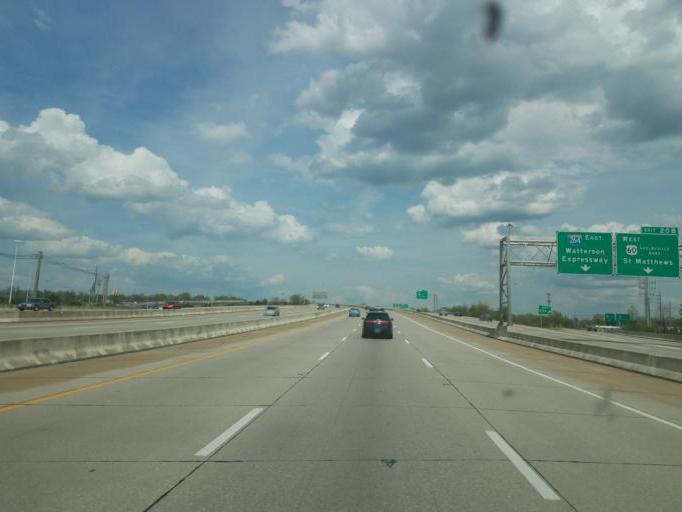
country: US
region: Kentucky
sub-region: Jefferson County
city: Beechwood Village
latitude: 38.2447
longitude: -85.6207
